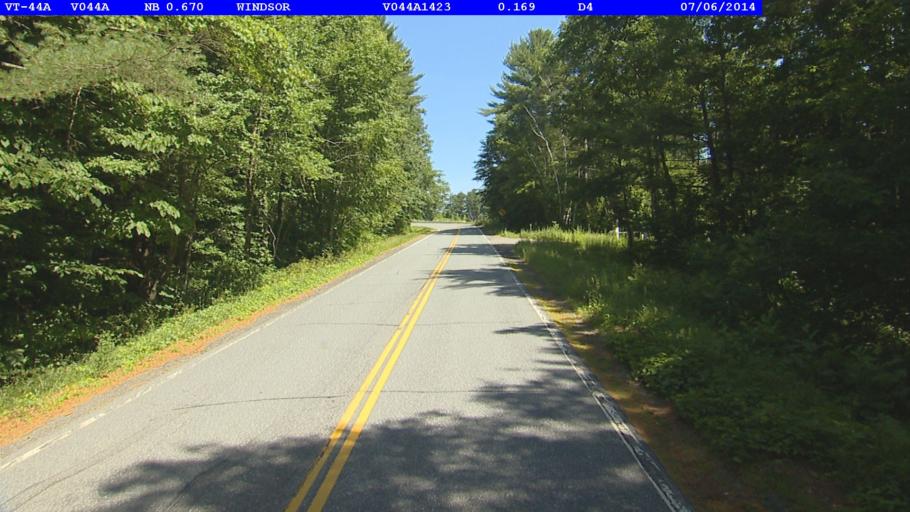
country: US
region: Vermont
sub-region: Windsor County
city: Windsor
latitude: 43.4319
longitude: -72.4014
